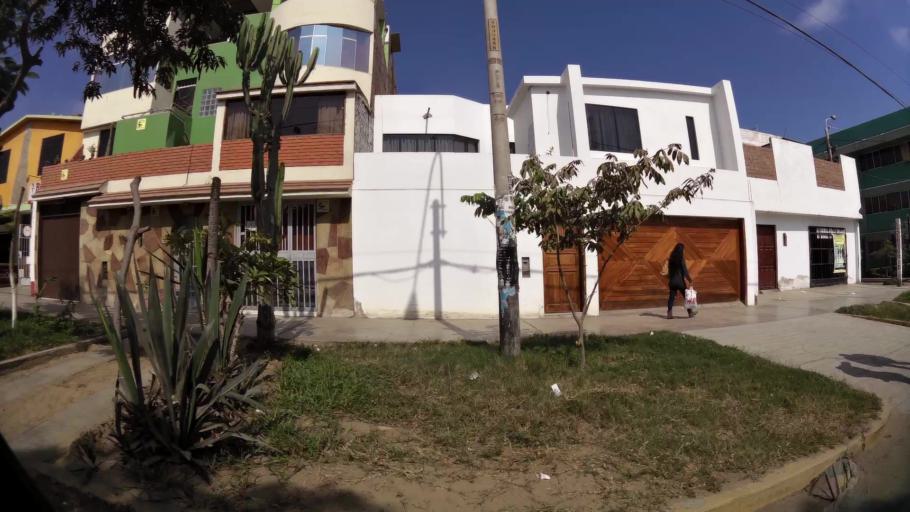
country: PE
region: La Libertad
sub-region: Provincia de Trujillo
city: Trujillo
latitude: -8.1217
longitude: -79.0422
